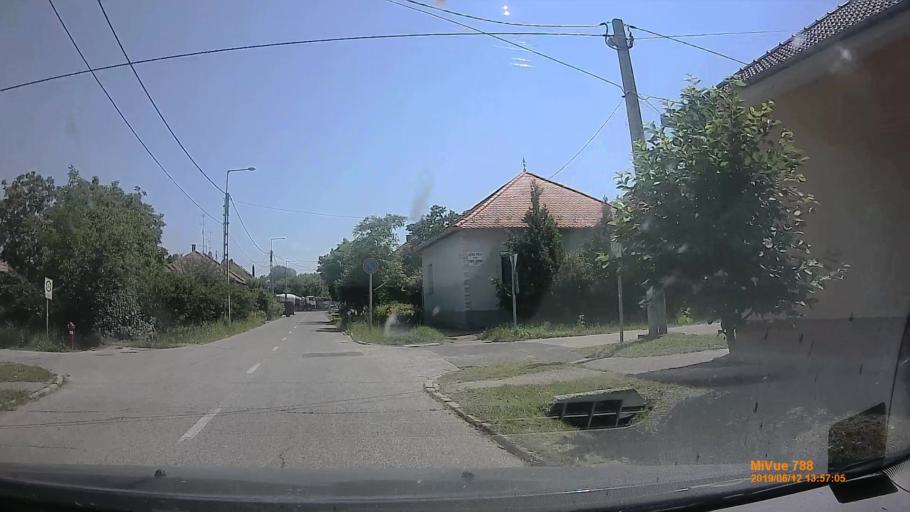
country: HU
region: Csongrad
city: Szeged
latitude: 46.2603
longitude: 20.1815
